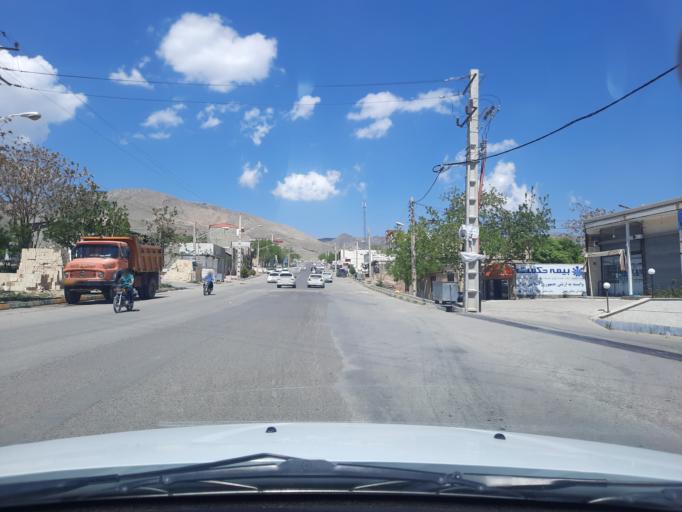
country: IR
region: Qazvin
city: Qazvin
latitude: 36.3312
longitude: 50.1503
